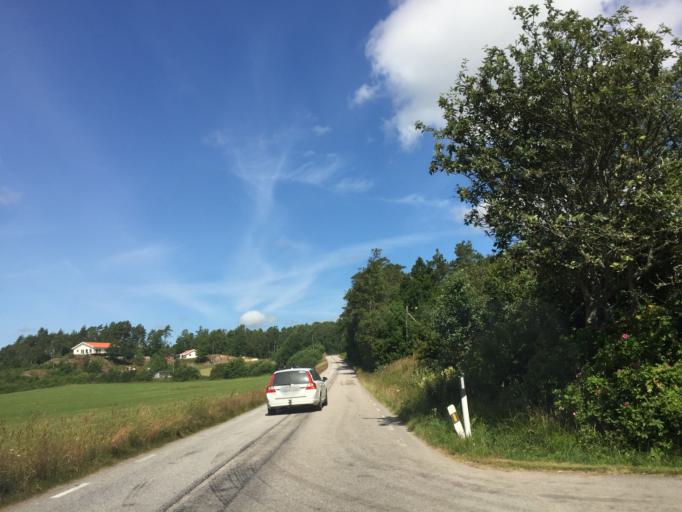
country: SE
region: Vaestra Goetaland
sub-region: Orust
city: Henan
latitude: 58.2823
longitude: 11.5850
